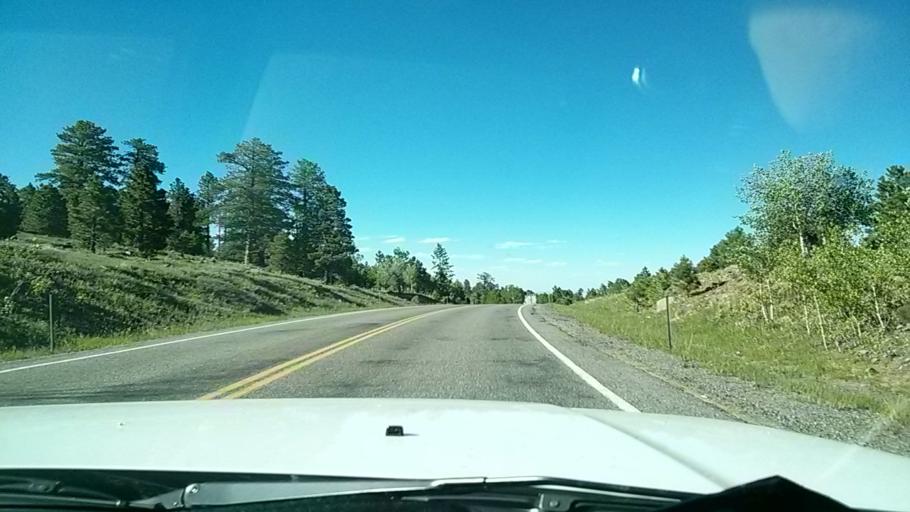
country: US
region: Utah
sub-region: Wayne County
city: Loa
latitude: 38.1264
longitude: -111.3292
